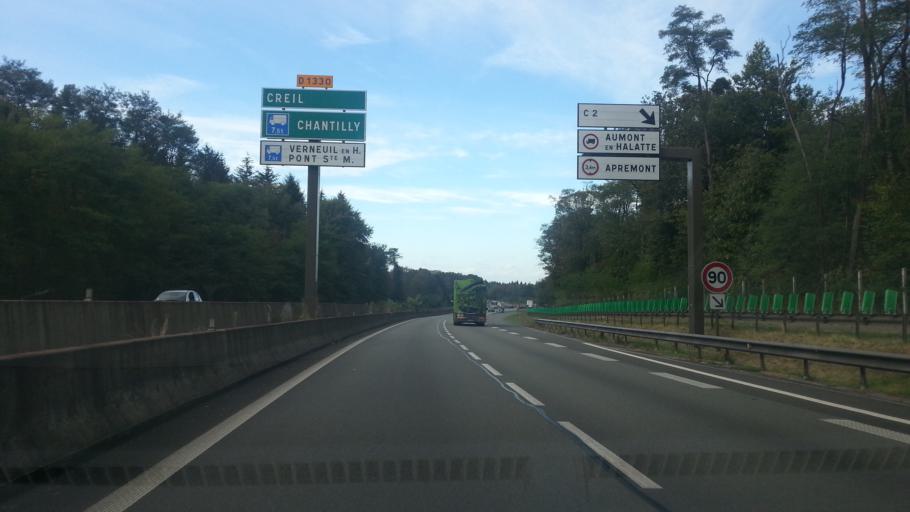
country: FR
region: Picardie
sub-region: Departement de l'Oise
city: Avilly-Saint-Leonard
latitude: 49.2278
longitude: 2.5413
